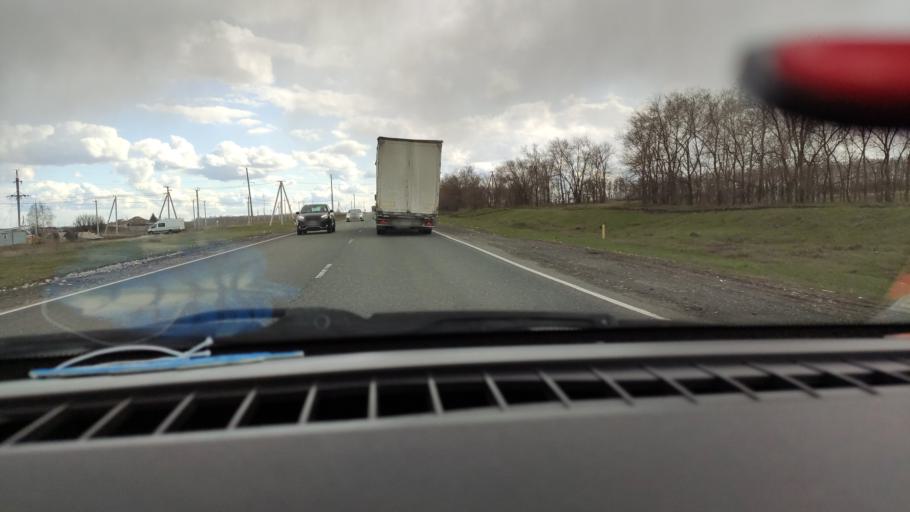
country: RU
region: Saratov
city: Balakovo
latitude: 52.1175
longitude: 47.7515
